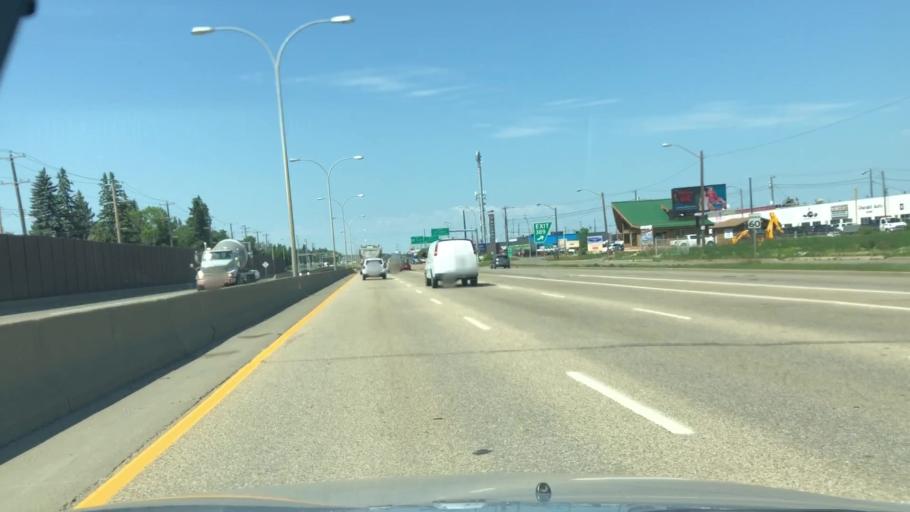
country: CA
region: Alberta
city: Edmonton
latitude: 53.5814
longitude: -113.4864
